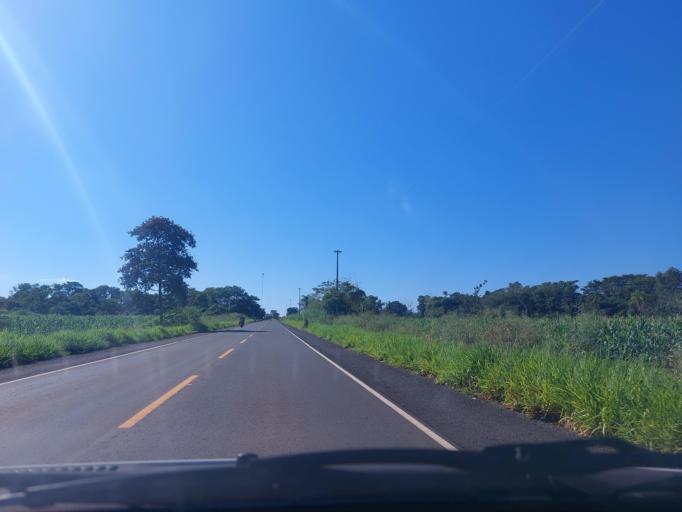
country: PY
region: San Pedro
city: Guayaybi
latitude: -24.3176
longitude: -56.1774
